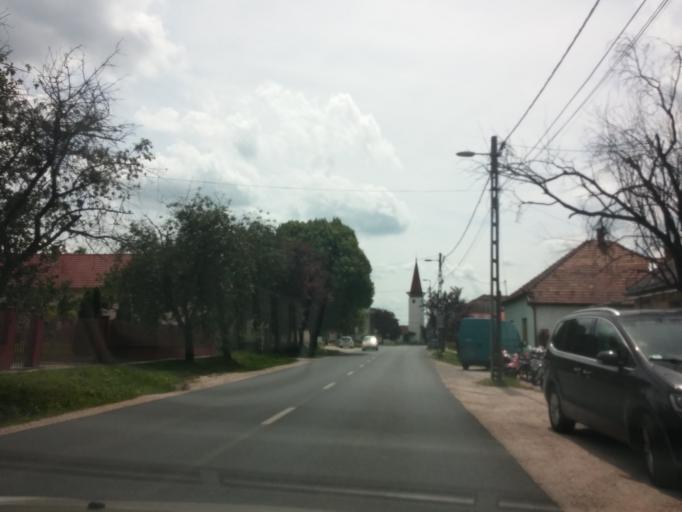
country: HU
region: Pest
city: Toekoel
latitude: 47.3245
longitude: 18.9638
